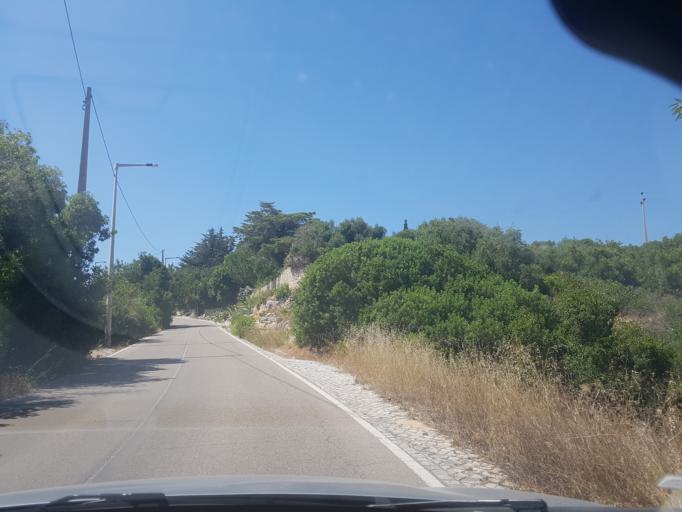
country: PT
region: Faro
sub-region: Lagoa
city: Carvoeiro
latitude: 37.0910
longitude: -8.4413
